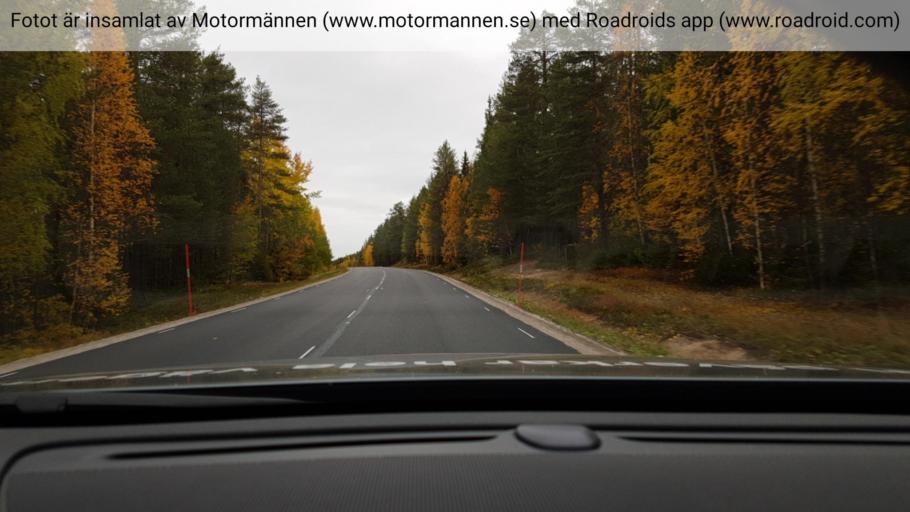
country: SE
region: Norrbotten
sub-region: Overkalix Kommun
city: OEverkalix
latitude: 66.4681
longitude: 22.7926
